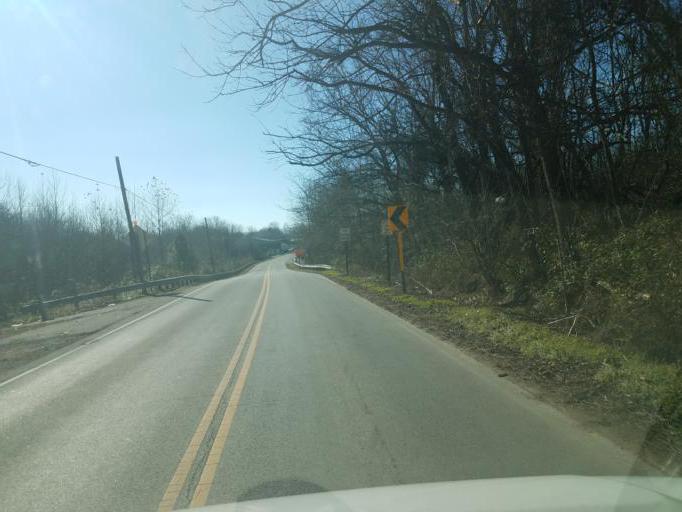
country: US
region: Ohio
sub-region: Scioto County
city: Sciotodale
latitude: 38.7717
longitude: -82.8783
